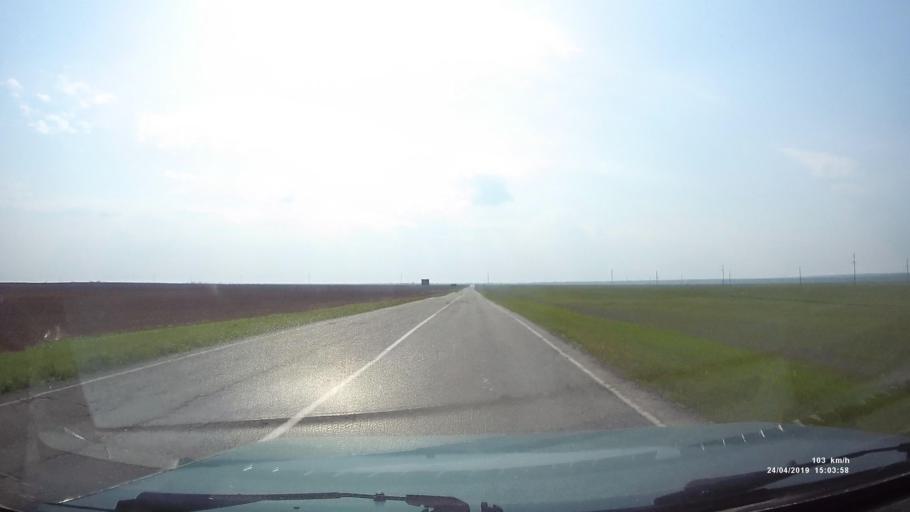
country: RU
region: Rostov
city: Remontnoye
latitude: 46.5637
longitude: 43.4808
